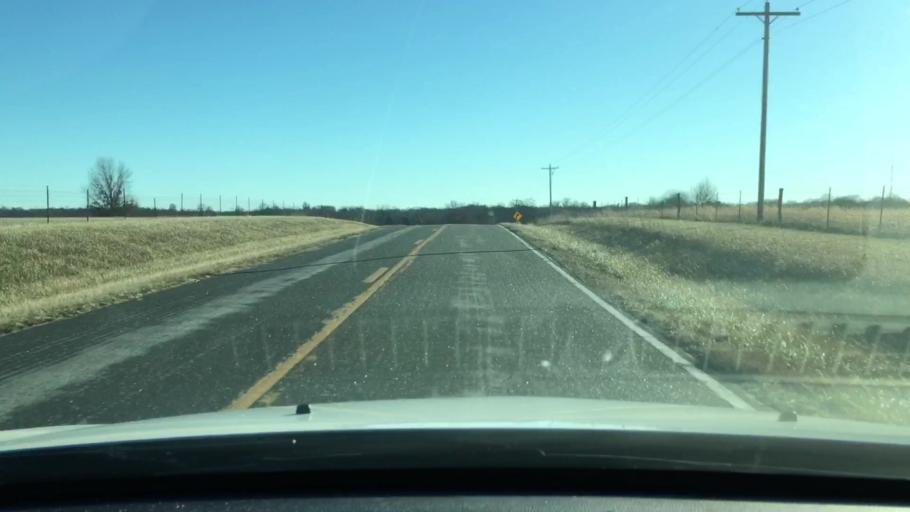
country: US
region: Missouri
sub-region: Audrain County
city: Mexico
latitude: 39.2627
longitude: -91.8288
